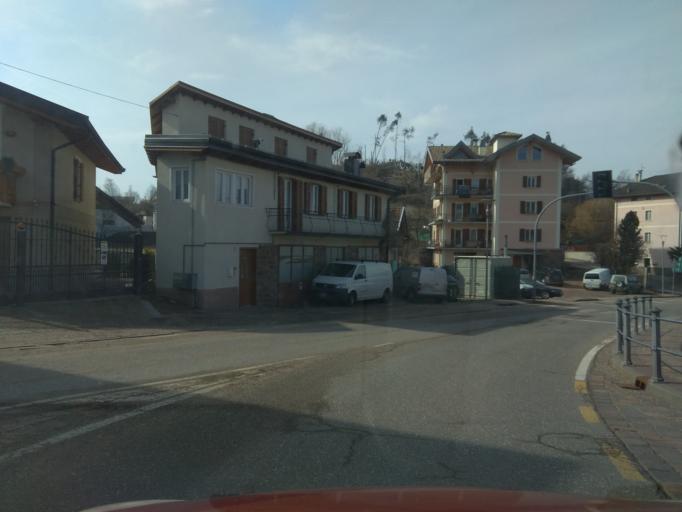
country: IT
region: Trentino-Alto Adige
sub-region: Provincia di Trento
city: Baselga di Pine
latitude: 46.1299
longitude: 11.2439
